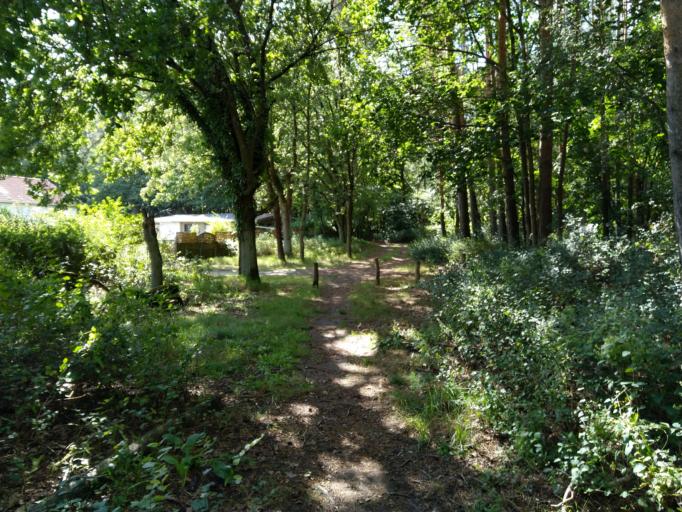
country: DE
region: Brandenburg
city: Schoneiche
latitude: 52.4559
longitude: 13.6984
